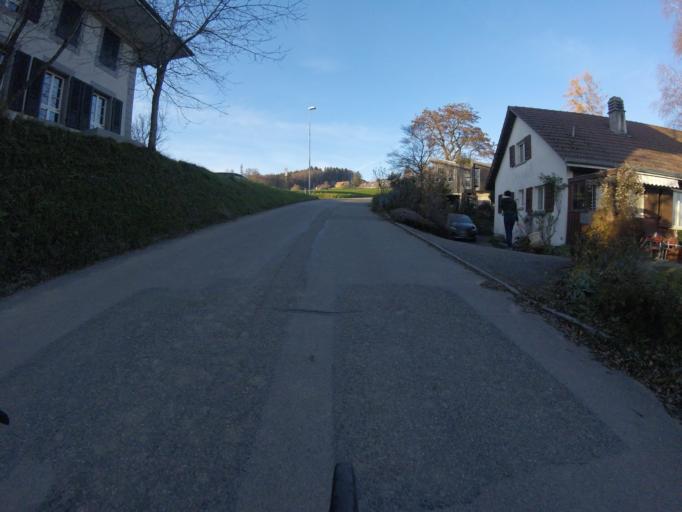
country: CH
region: Bern
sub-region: Bern-Mittelland District
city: Muhleberg
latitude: 46.9374
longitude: 7.2869
